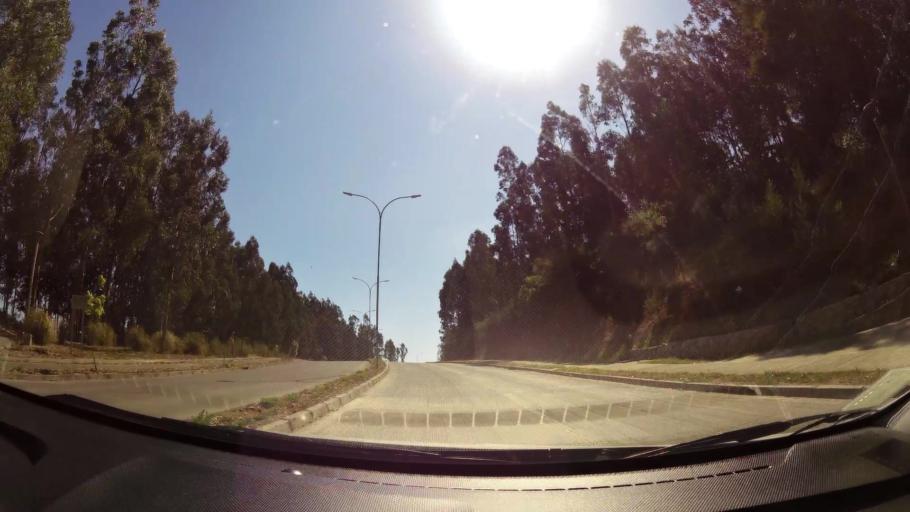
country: CL
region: Biobio
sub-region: Provincia de Concepcion
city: Concepcion
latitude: -36.7873
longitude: -73.0346
